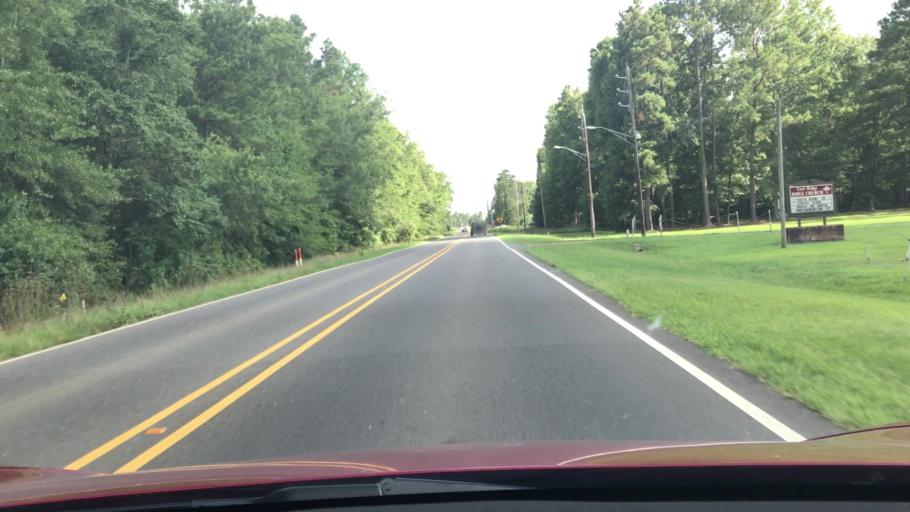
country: US
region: Louisiana
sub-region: Bossier Parish
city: Bossier City
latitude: 32.3934
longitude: -93.7386
